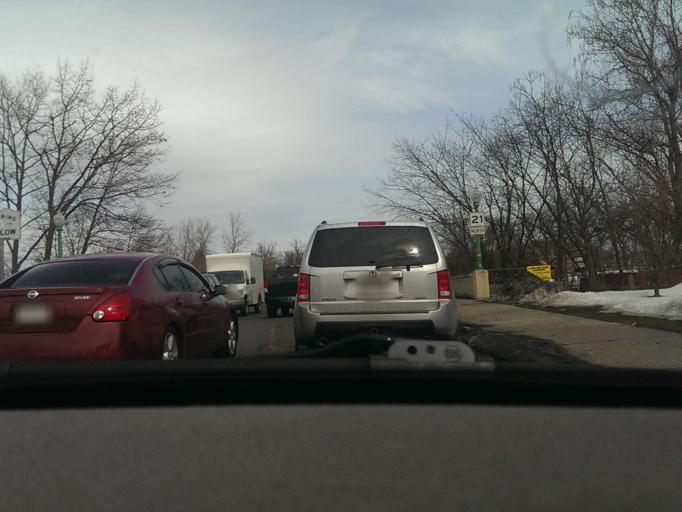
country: US
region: Massachusetts
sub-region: Hampden County
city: Ludlow
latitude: 42.1558
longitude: -72.4851
